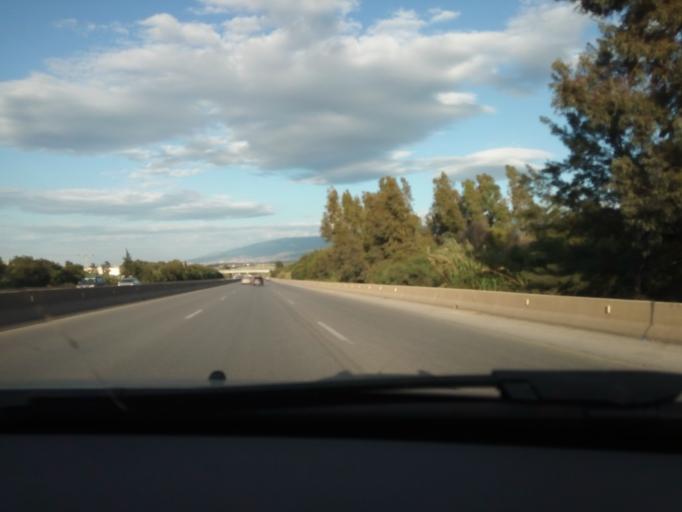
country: DZ
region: Tipaza
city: El Affroun
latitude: 36.4460
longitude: 2.6335
